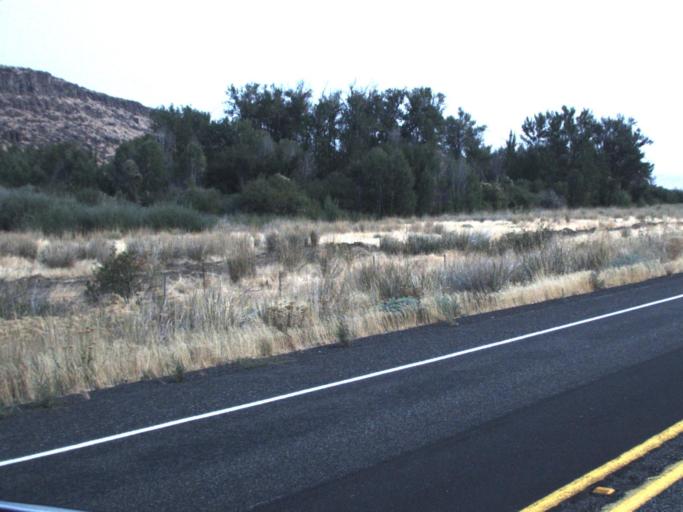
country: US
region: Washington
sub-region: Yakima County
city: Toppenish
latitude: 46.2219
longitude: -120.4312
